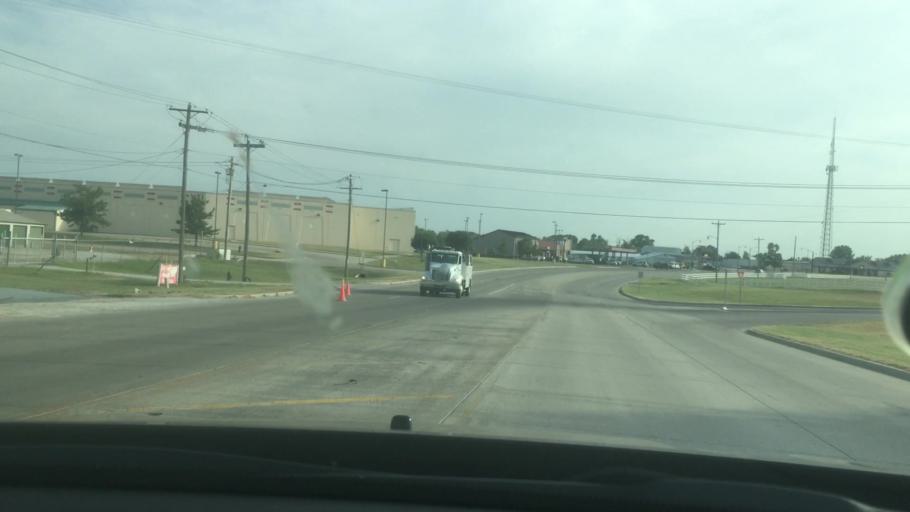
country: US
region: Oklahoma
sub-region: Pontotoc County
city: Ada
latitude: 34.7709
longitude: -96.6988
